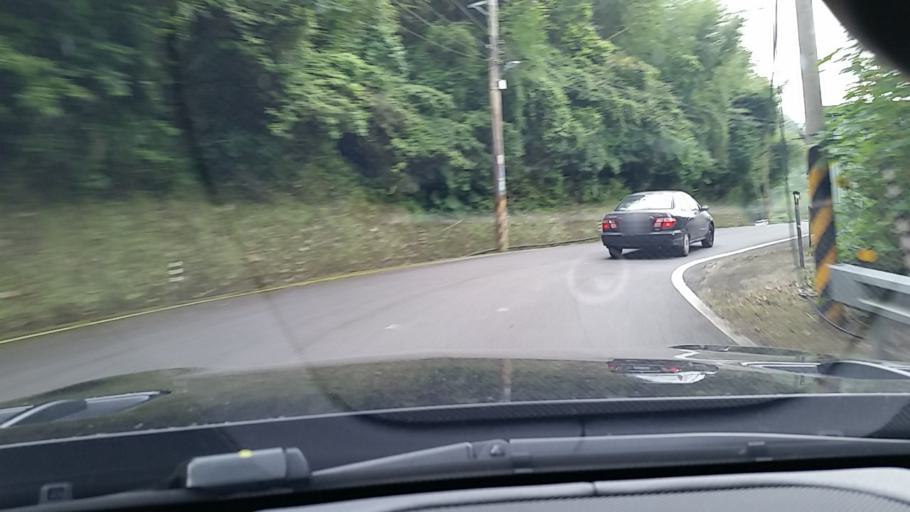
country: TW
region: Taiwan
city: Daxi
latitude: 24.7993
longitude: 121.2896
